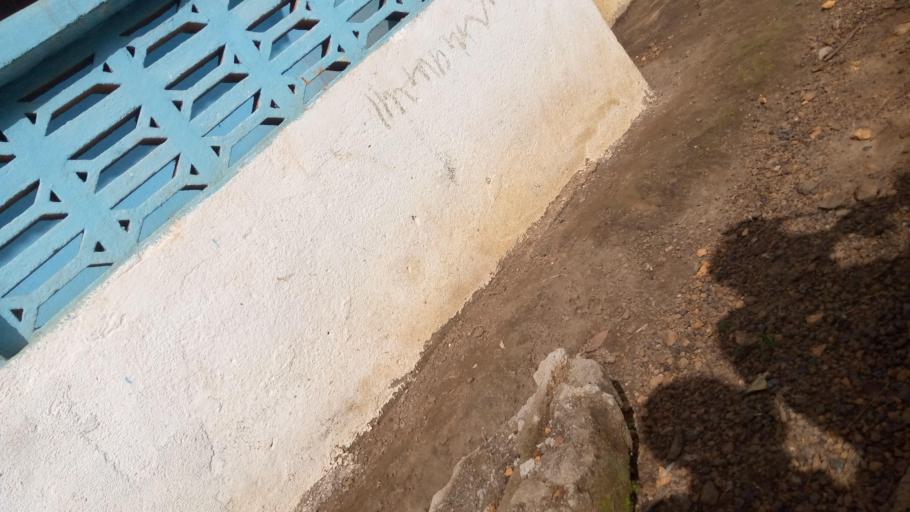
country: SL
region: Southern Province
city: Pujehun
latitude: 7.3581
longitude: -11.7250
